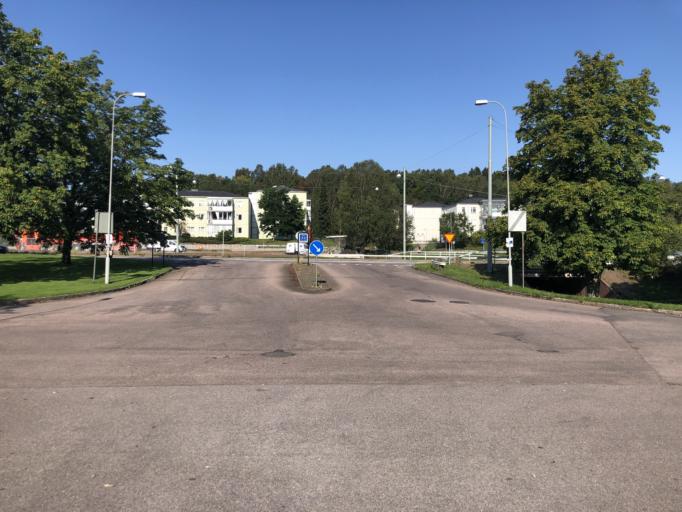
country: SE
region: Vaestra Goetaland
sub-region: Goteborg
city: Goeteborg
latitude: 57.7452
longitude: 11.9783
